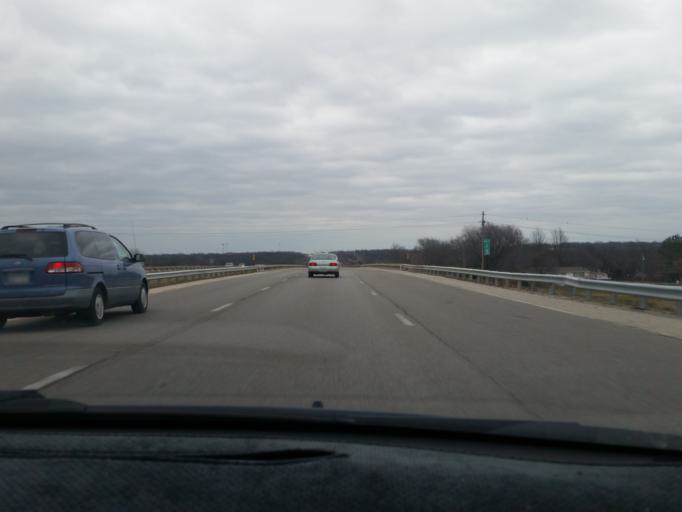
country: US
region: Kansas
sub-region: Johnson County
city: De Soto
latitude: 38.9607
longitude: -94.9846
